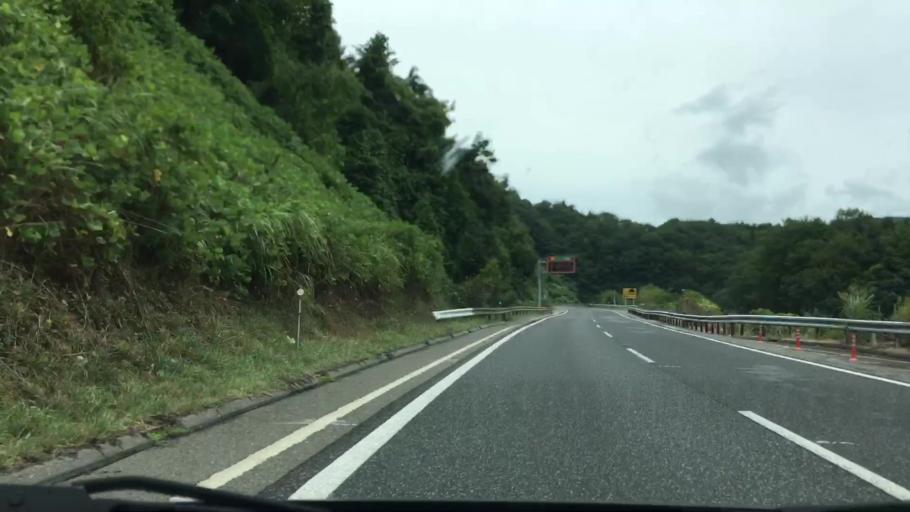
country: JP
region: Okayama
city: Niimi
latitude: 34.9808
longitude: 133.6155
